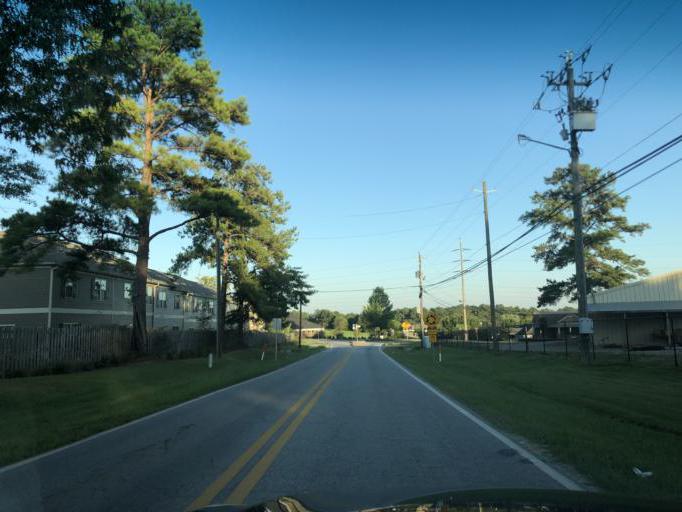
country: US
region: Georgia
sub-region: Muscogee County
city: Columbus
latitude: 32.5476
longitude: -84.8914
